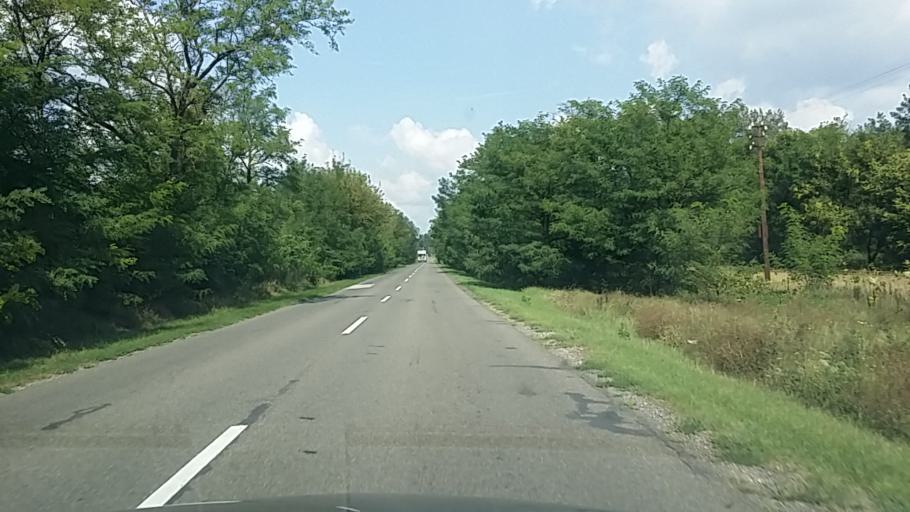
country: HU
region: Bacs-Kiskun
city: Lakitelek
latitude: 46.8535
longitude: 19.9805
